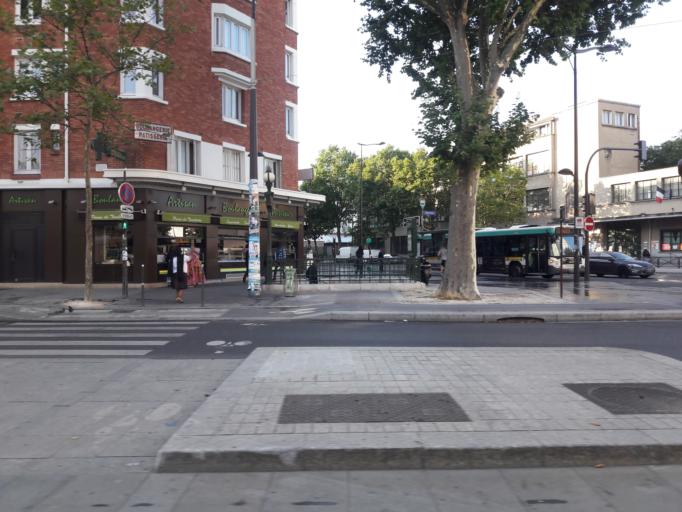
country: FR
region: Ile-de-France
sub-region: Departement du Val-de-Marne
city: Le Kremlin-Bicetre
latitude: 48.8214
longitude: 2.3696
